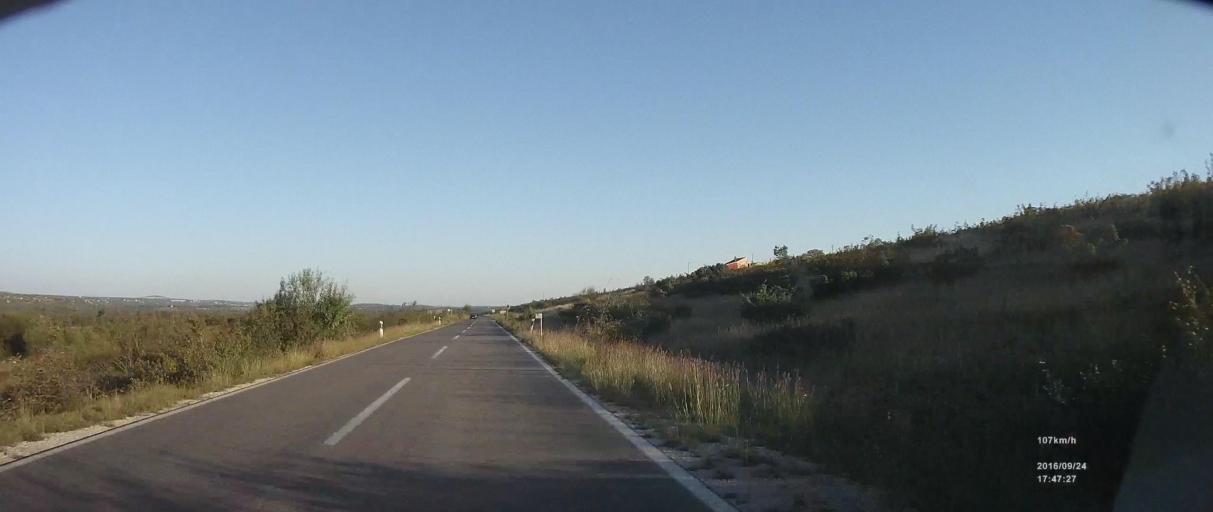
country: HR
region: Zadarska
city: Polaca
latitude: 44.0753
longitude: 15.5229
